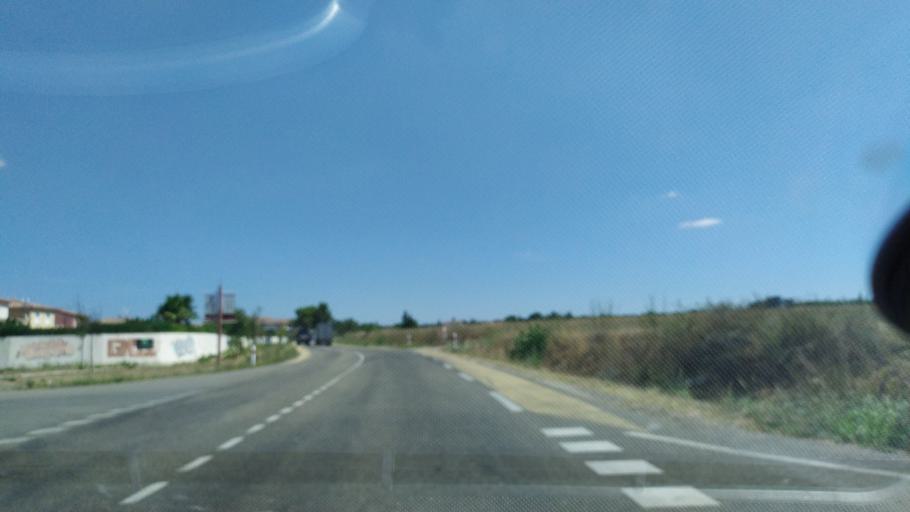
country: FR
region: Languedoc-Roussillon
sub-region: Departement du Gard
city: Caissargues
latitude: 43.7917
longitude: 4.3730
